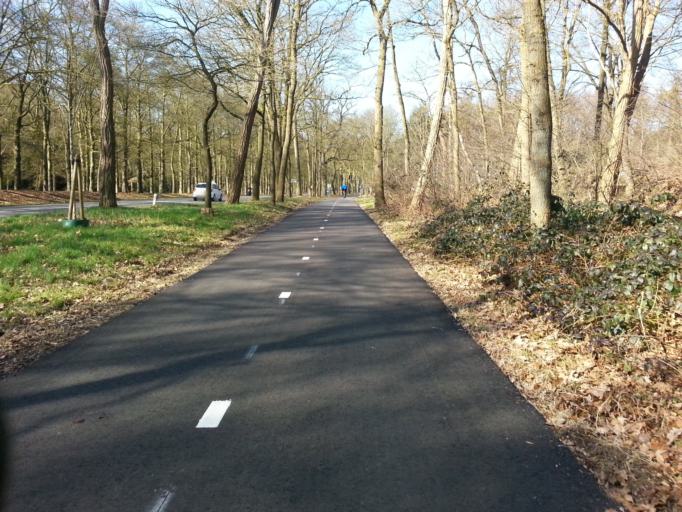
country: NL
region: Utrecht
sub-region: Gemeente Utrechtse Heuvelrug
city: Maarsbergen
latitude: 52.0270
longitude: 5.3860
